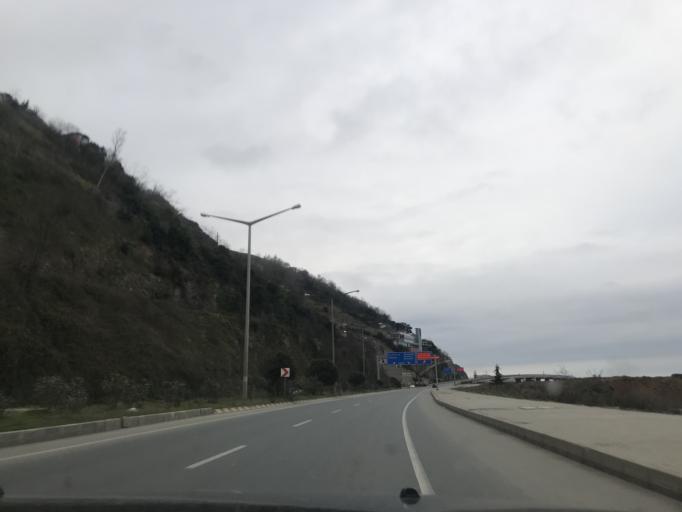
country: TR
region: Trabzon
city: Derecik
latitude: 40.9988
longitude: 39.6405
